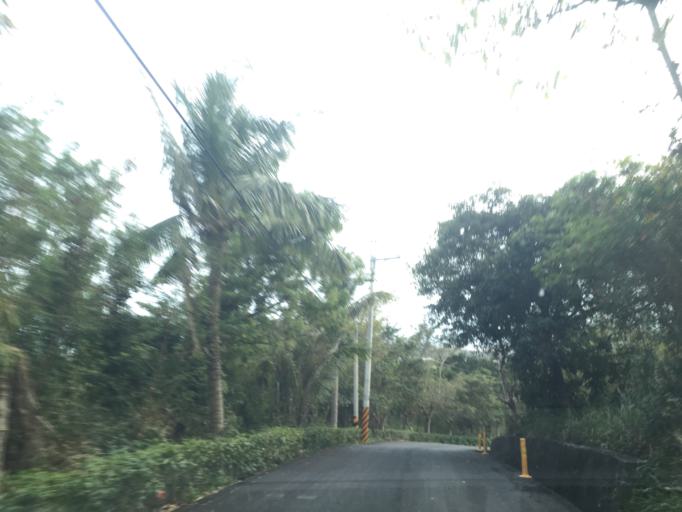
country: TW
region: Taiwan
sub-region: Taitung
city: Taitung
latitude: 22.7904
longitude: 121.1608
